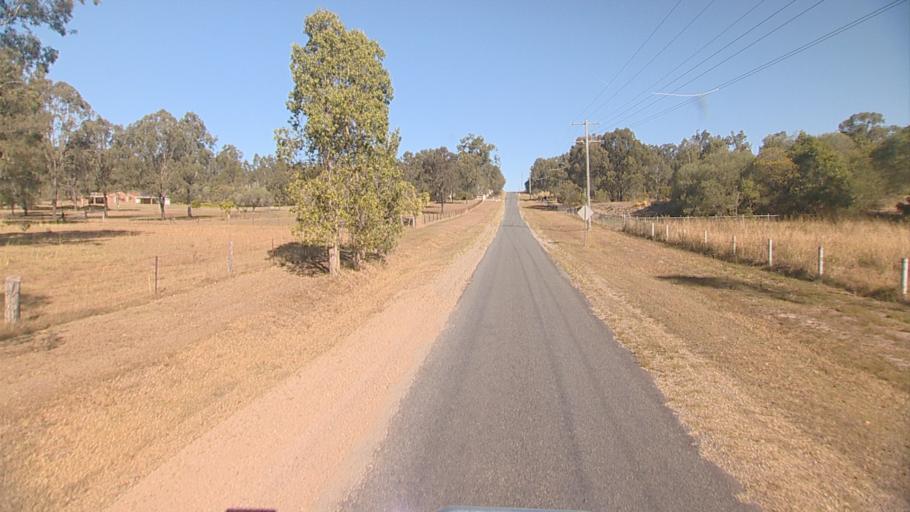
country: AU
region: Queensland
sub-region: Logan
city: Cedar Vale
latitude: -27.8578
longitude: 153.0273
